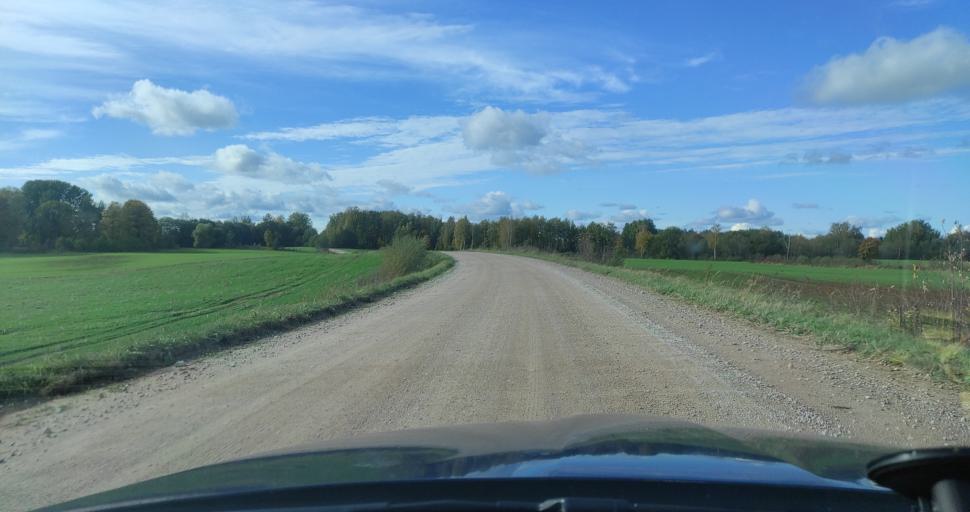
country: LV
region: Jaunpils
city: Jaunpils
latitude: 56.8309
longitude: 22.9853
